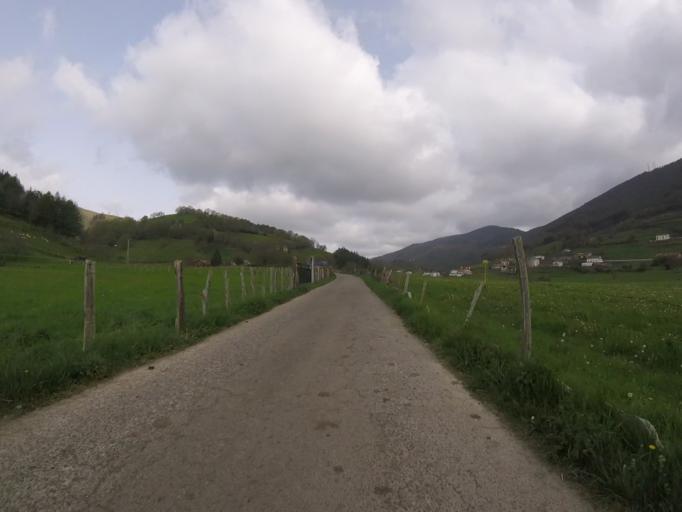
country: ES
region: Basque Country
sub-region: Provincia de Guipuzcoa
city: Berastegui
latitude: 43.1248
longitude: -1.9851
